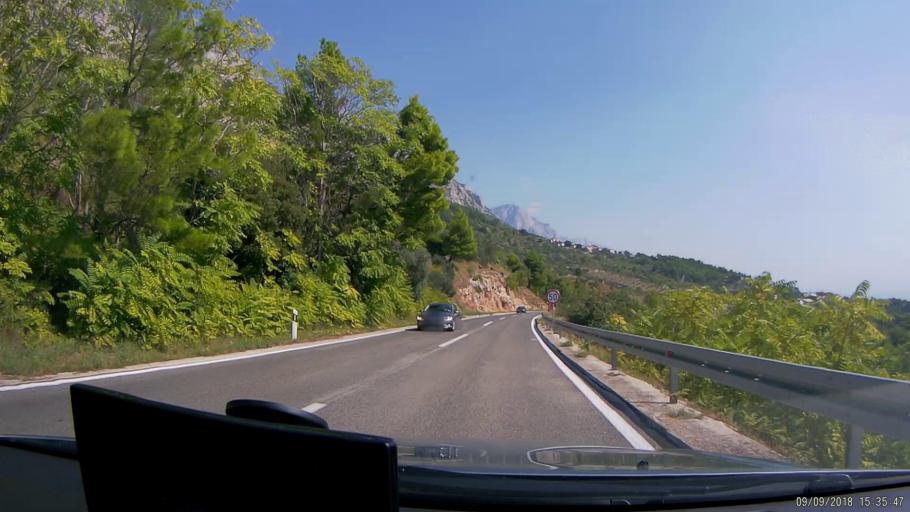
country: HR
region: Splitsko-Dalmatinska
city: Donja Brela
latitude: 43.3826
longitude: 16.9189
